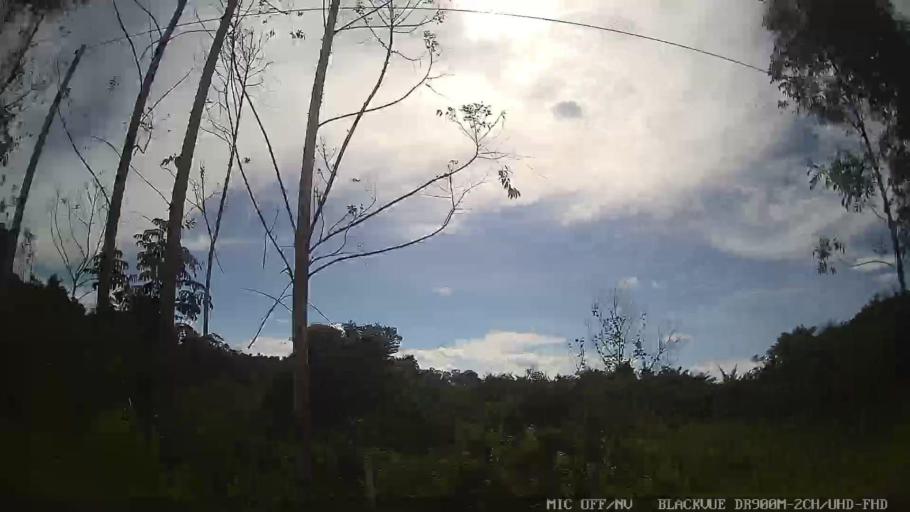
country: BR
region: Sao Paulo
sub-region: Conchas
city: Conchas
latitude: -22.9615
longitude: -47.9815
